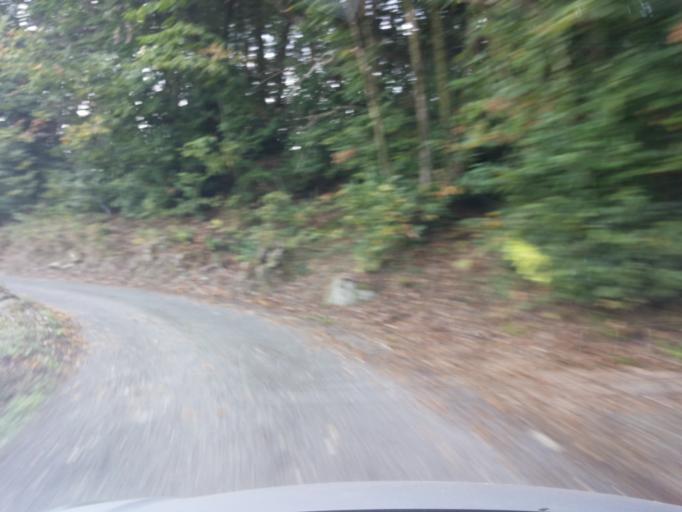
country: IT
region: Piedmont
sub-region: Provincia di Biella
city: Roppolo
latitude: 45.4261
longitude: 8.0795
